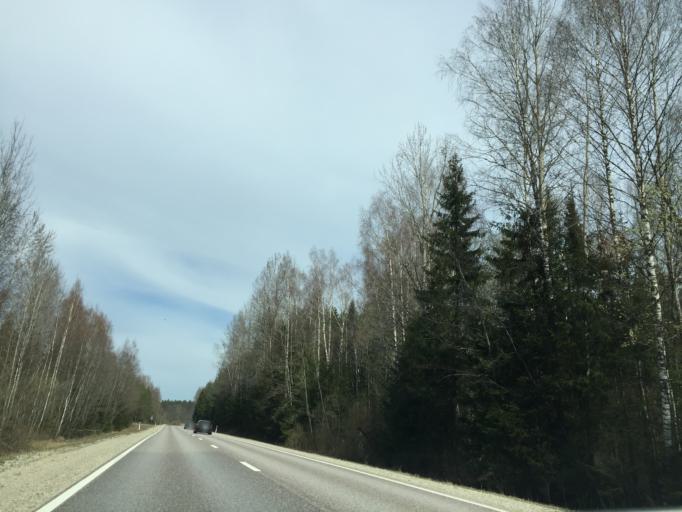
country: LV
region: Valkas Rajons
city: Valka
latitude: 57.7206
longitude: 25.9343
